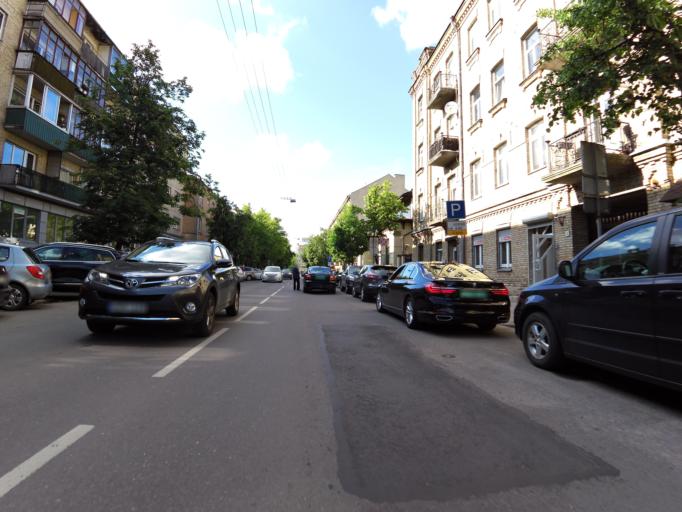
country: LT
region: Vilnius County
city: Naujamiestis
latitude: 54.6801
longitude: 25.2700
